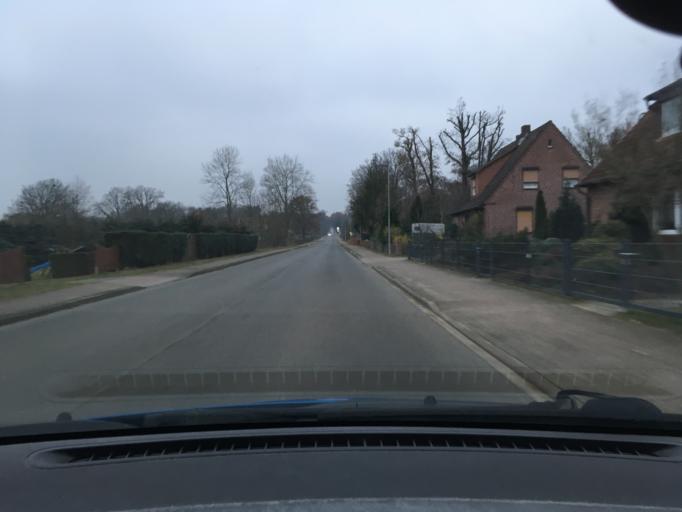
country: DE
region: Lower Saxony
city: Bispingen
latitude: 53.1132
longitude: 9.9586
